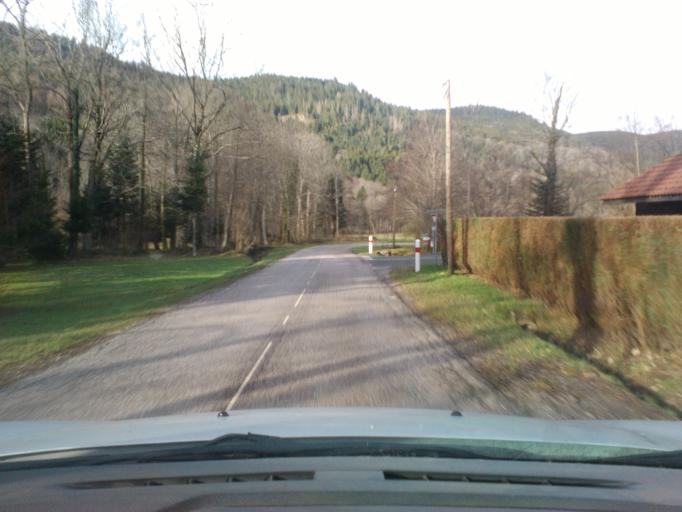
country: FR
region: Lorraine
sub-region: Departement des Vosges
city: Xonrupt-Longemer
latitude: 48.1213
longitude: 6.9537
